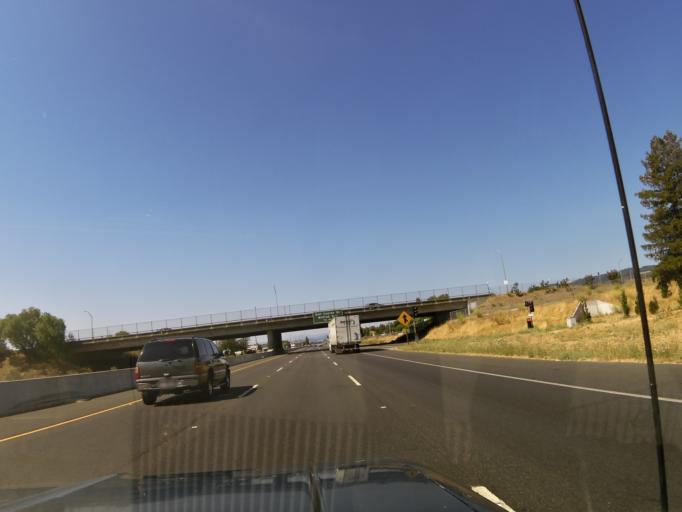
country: US
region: California
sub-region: Sonoma County
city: Rohnert Park
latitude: 38.3472
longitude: -122.7130
